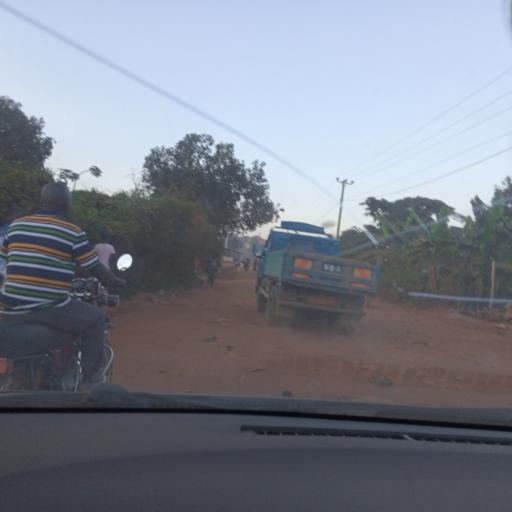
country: UG
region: Central Region
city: Masaka
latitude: -0.3206
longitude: 31.7654
